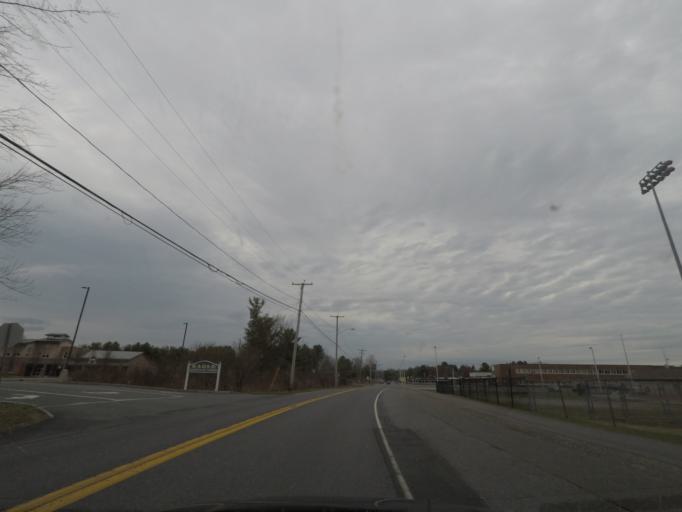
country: US
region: New York
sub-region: Albany County
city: Delmar
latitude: 42.6093
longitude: -73.8578
